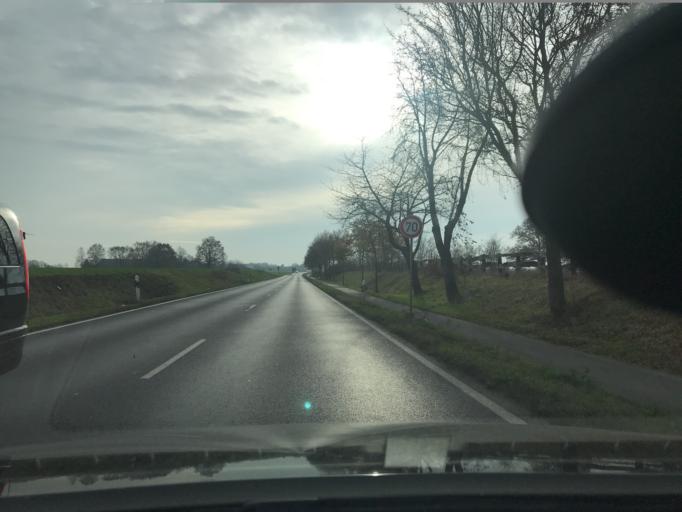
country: DE
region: North Rhine-Westphalia
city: Kempen
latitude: 51.3829
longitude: 6.4657
